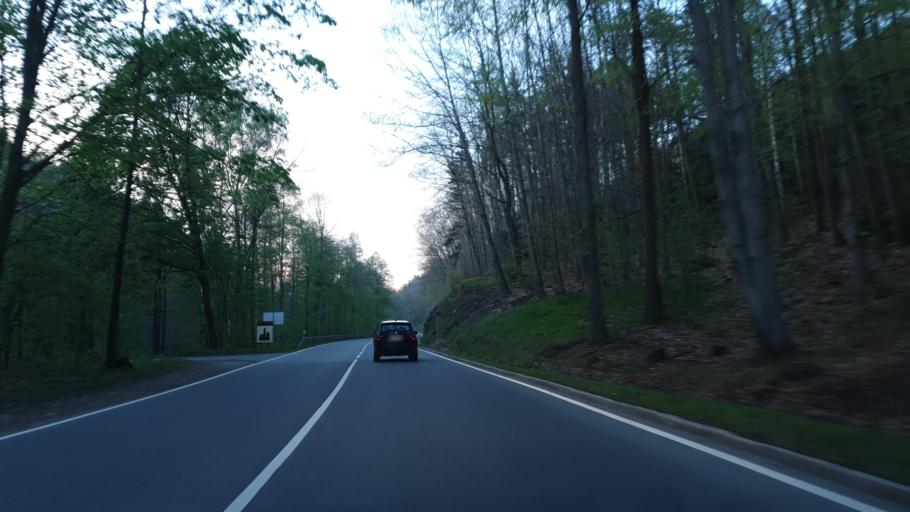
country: DE
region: Saxony
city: Aue
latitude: 50.6003
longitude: 12.7166
